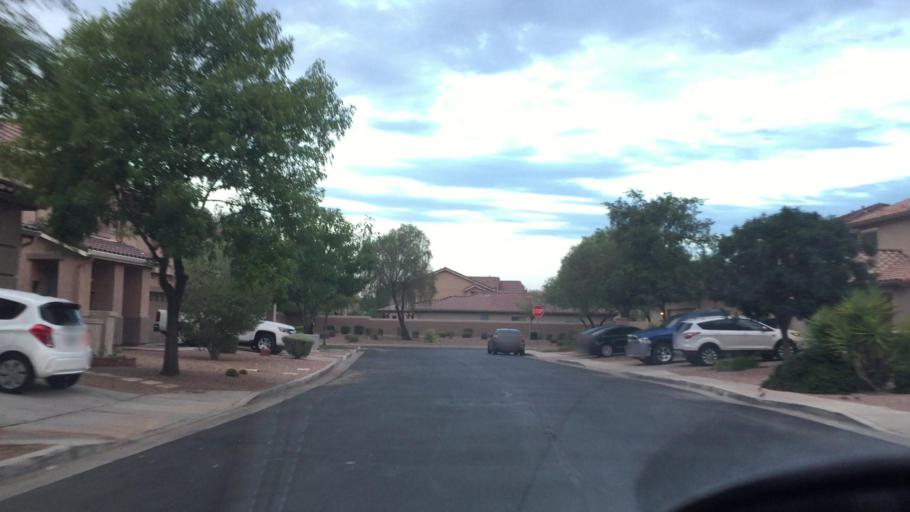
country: US
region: Arizona
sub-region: Maricopa County
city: Gilbert
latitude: 33.3236
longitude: -111.7098
